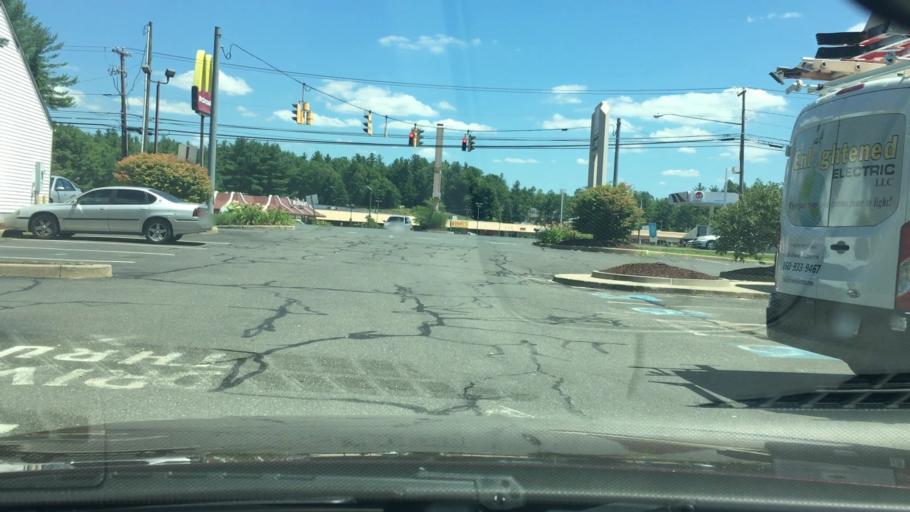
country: US
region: Connecticut
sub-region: Tolland County
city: Stafford Springs
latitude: 41.9688
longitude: -72.3319
